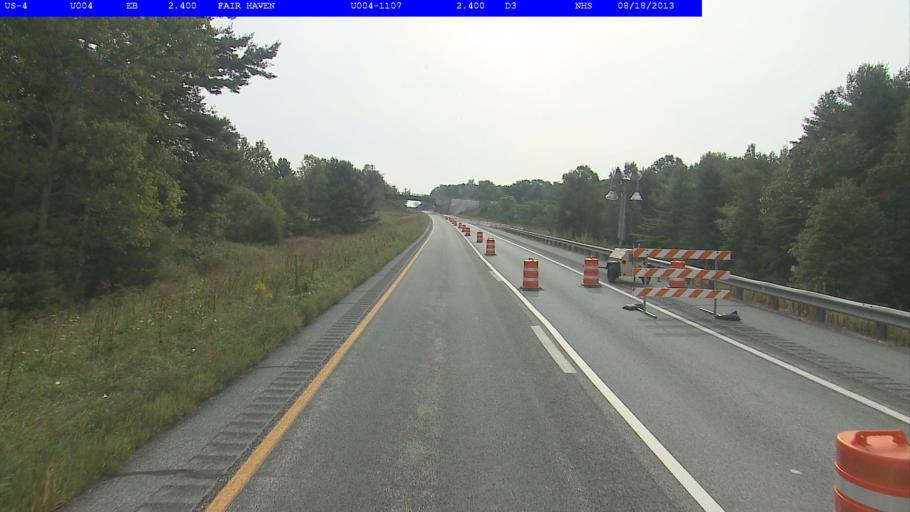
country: US
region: Vermont
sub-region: Rutland County
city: Fair Haven
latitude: 43.6050
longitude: -73.2635
